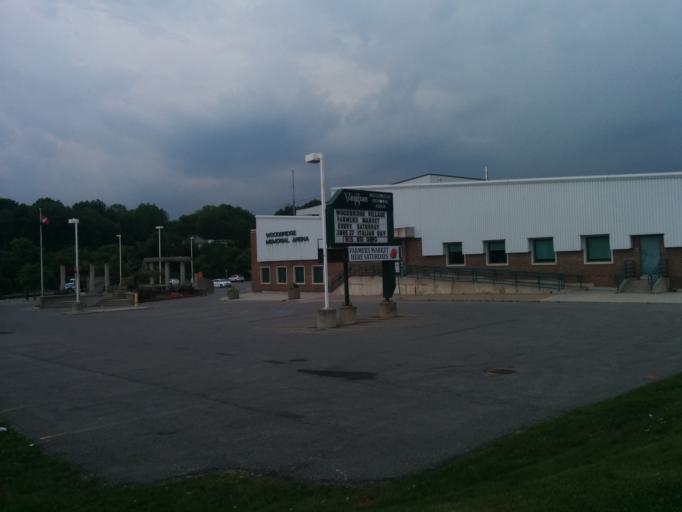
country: CA
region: Ontario
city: Vaughan
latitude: 43.7807
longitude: -79.5898
